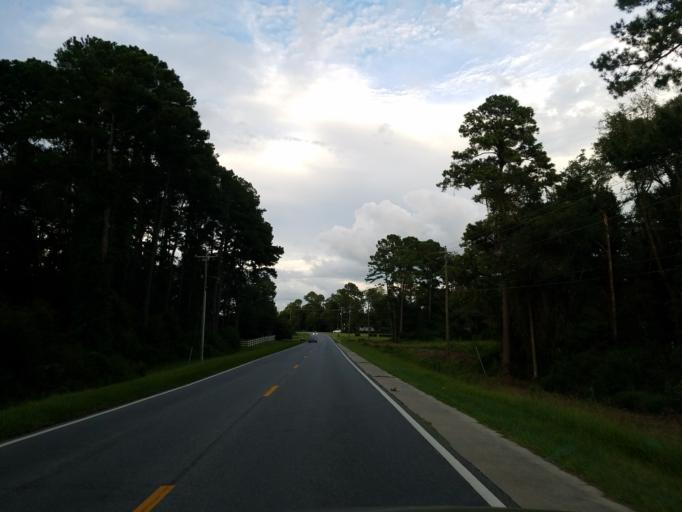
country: US
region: Georgia
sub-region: Cook County
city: Adel
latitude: 31.1485
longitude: -83.4215
